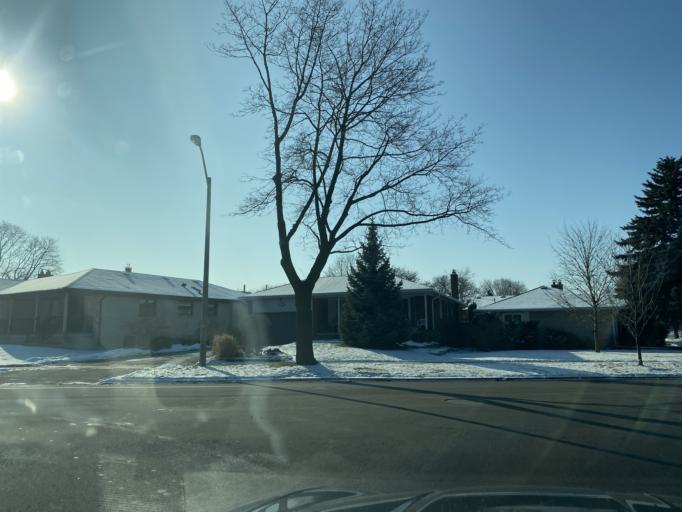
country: CA
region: Ontario
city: Etobicoke
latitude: 43.6626
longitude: -79.5674
